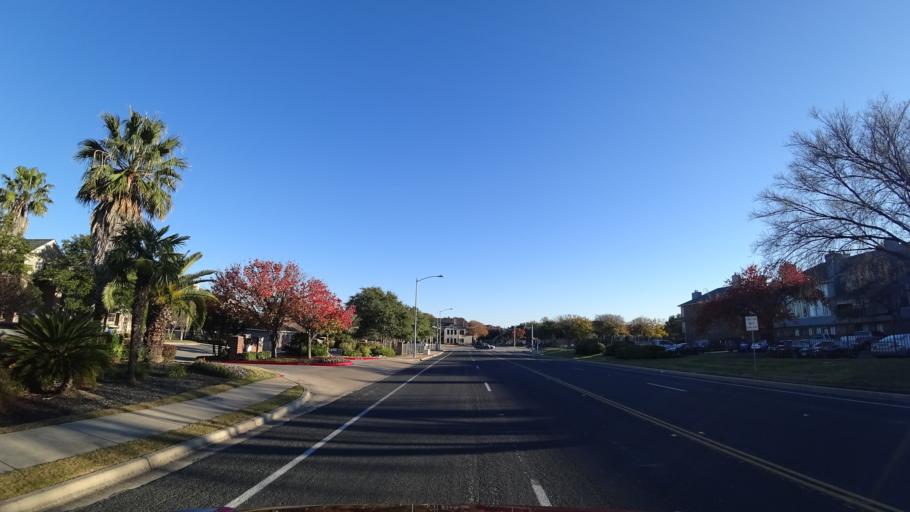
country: US
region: Texas
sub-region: Travis County
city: Wells Branch
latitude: 30.4115
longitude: -97.6960
